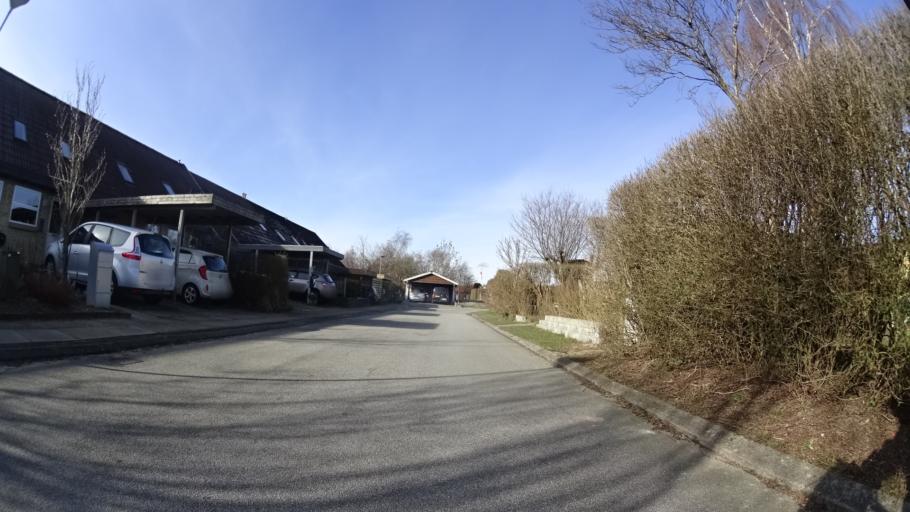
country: DK
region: Central Jutland
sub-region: Arhus Kommune
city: Tranbjerg
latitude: 56.0870
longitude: 10.1170
